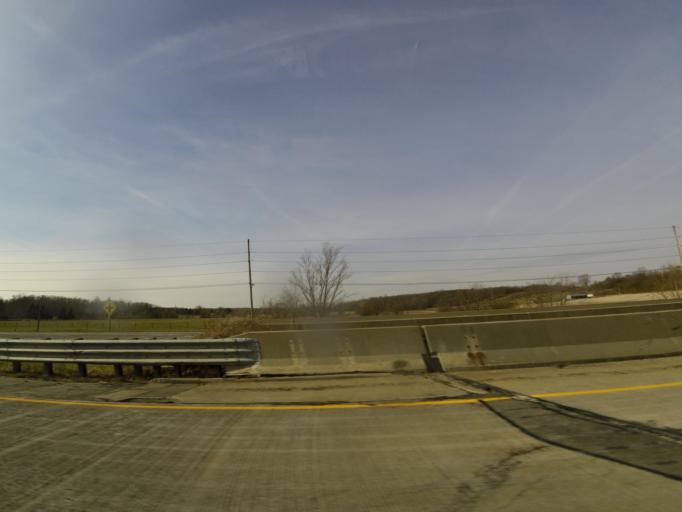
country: US
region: Illinois
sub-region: De Witt County
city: Clinton
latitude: 40.1054
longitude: -88.9652
